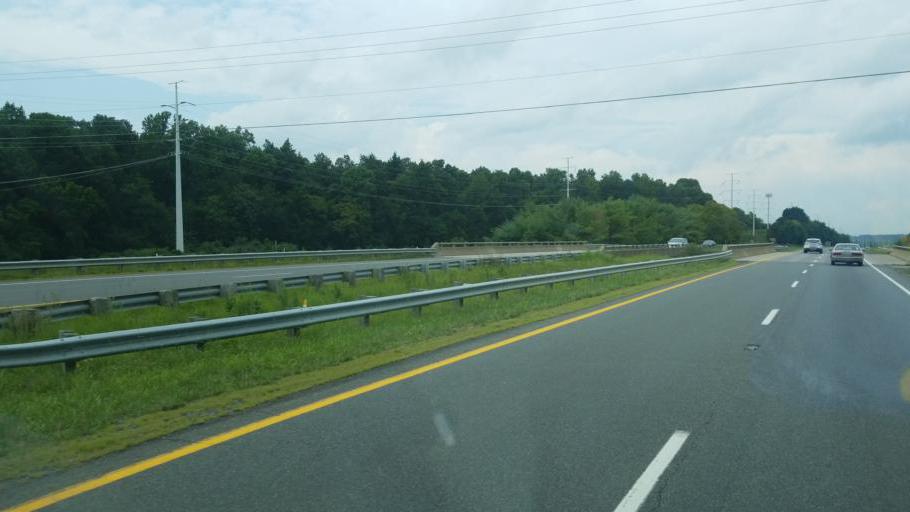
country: US
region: Virginia
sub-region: City of Winchester
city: Winchester
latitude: 39.1580
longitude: -78.2109
